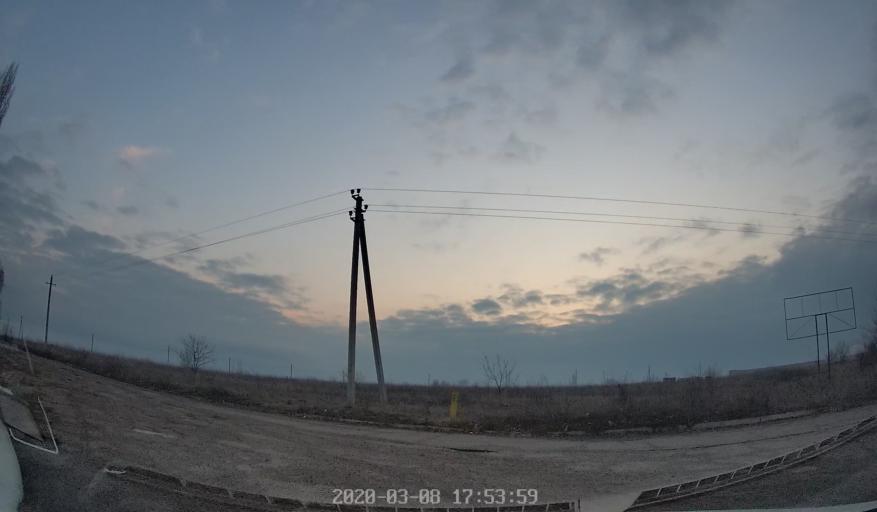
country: MD
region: Rezina
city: Rezina
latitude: 47.7539
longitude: 28.9492
